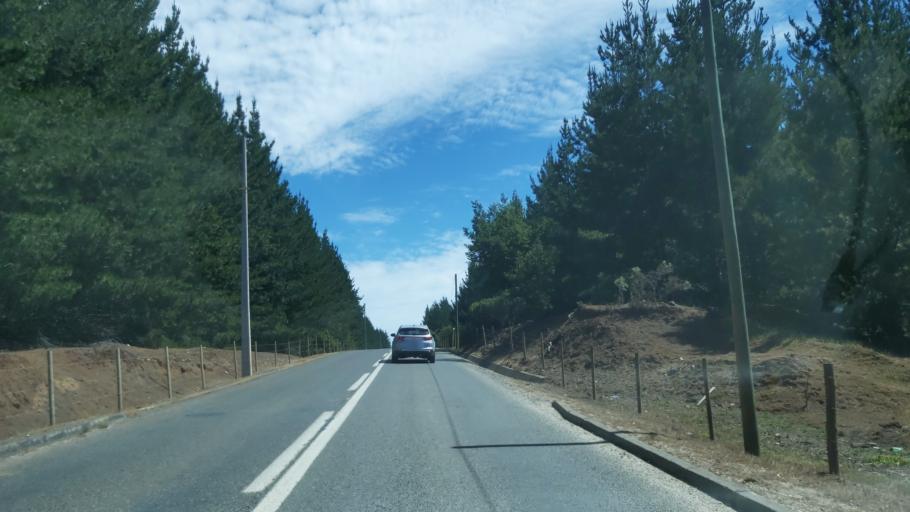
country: CL
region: Maule
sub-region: Provincia de Talca
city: Constitucion
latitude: -35.5282
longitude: -72.5401
